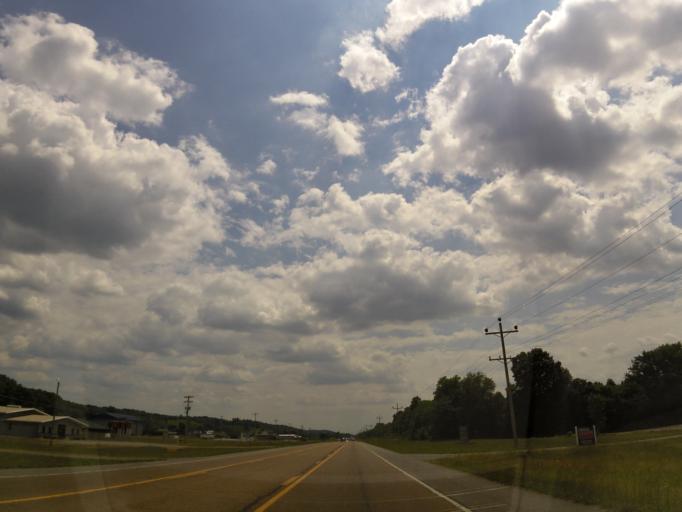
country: US
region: Tennessee
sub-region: Sequatchie County
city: Dunlap
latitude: 35.3423
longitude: -85.4110
